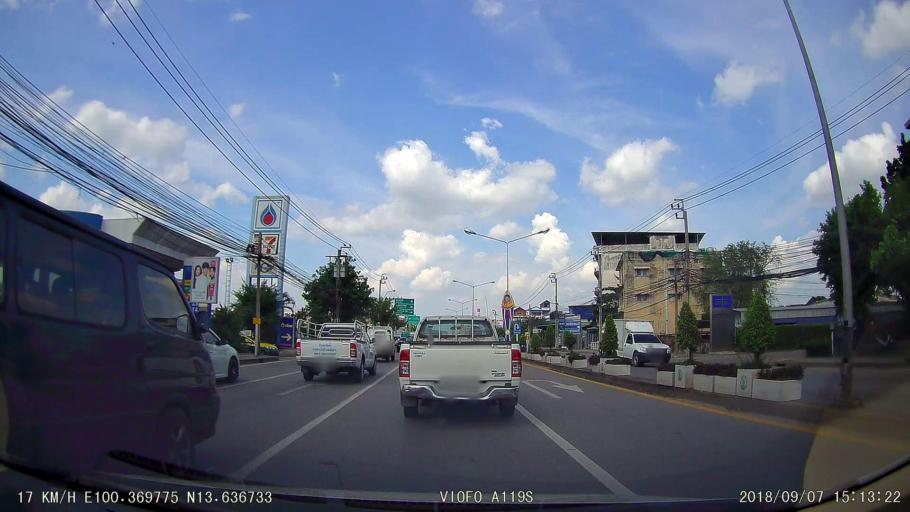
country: TH
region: Bangkok
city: Bang Bon
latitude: 13.6367
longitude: 100.3698
